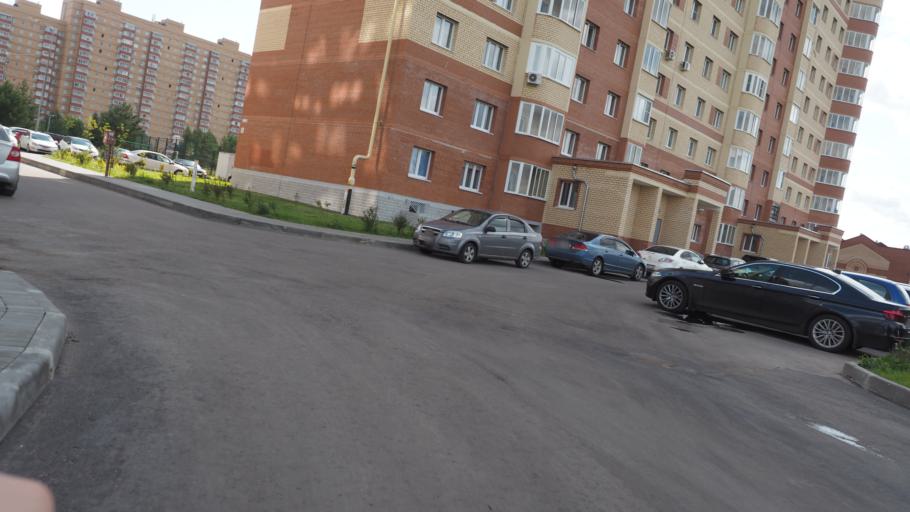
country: RU
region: Moskovskaya
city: Ramenskoye
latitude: 55.5949
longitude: 38.2496
